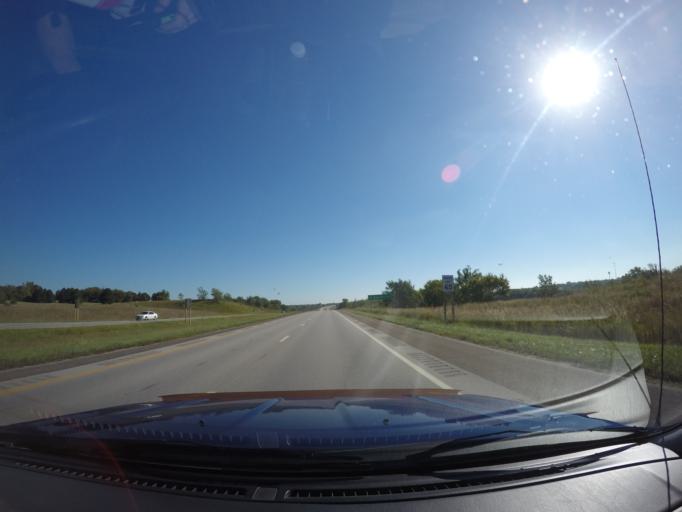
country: US
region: Kansas
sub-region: Pottawatomie County
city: Wamego
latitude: 39.2030
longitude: -96.4321
